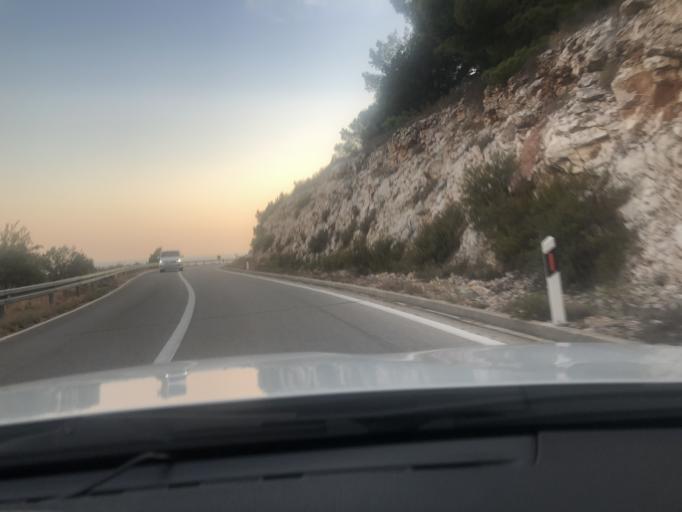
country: HR
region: Splitsko-Dalmatinska
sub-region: Grad Hvar
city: Hvar
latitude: 43.1615
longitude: 16.4924
